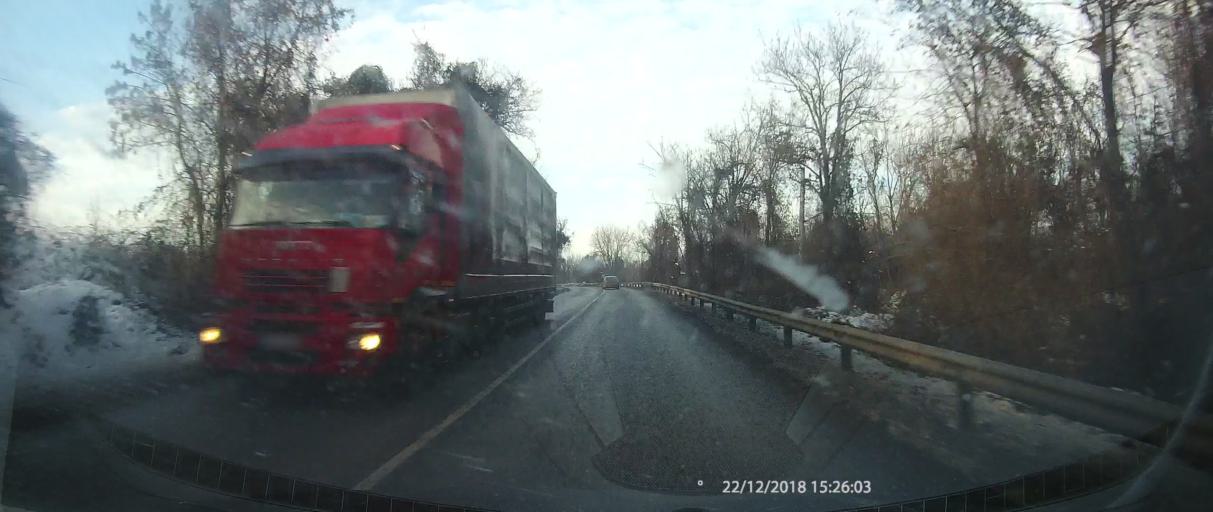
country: RO
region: Giurgiu
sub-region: Comuna Slobozia
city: Slobozia
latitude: 43.7669
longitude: 25.9013
